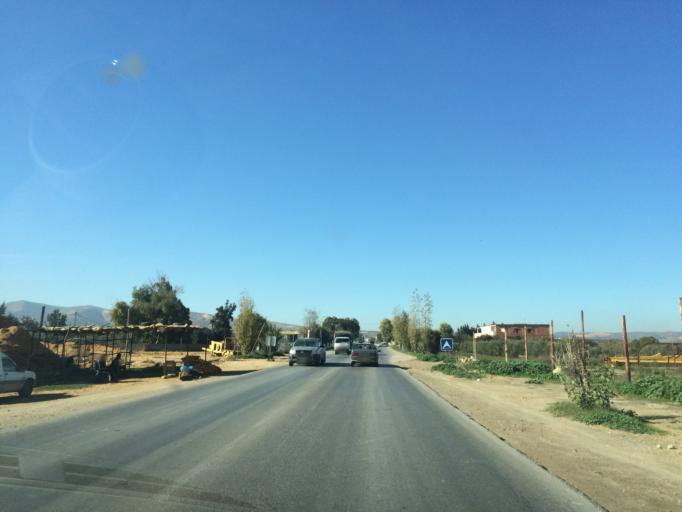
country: DZ
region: Relizane
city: Relizane
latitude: 35.9002
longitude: 0.5313
